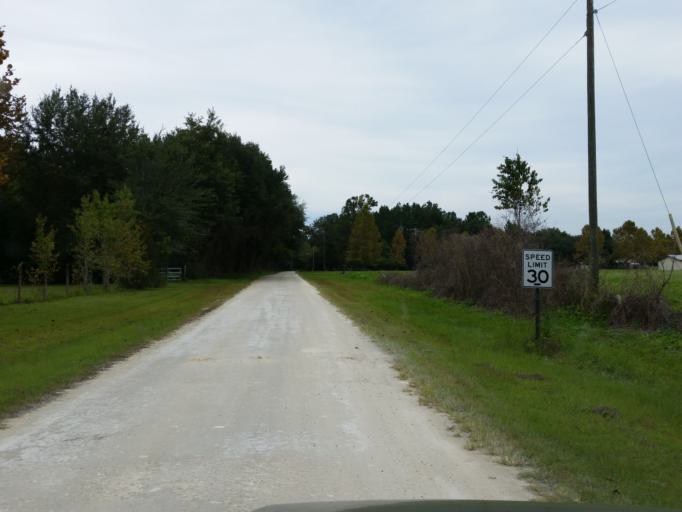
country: US
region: Florida
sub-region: Alachua County
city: High Springs
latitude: 29.9503
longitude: -82.5594
